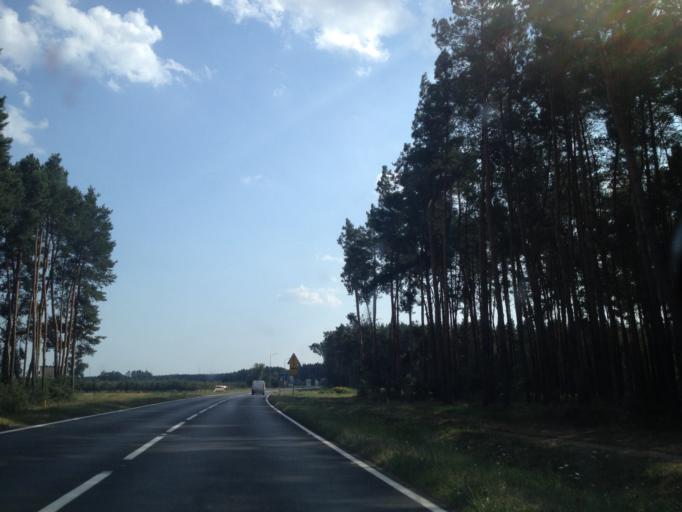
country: PL
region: Greater Poland Voivodeship
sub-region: Powiat poznanski
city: Kornik
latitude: 52.2219
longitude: 17.0736
